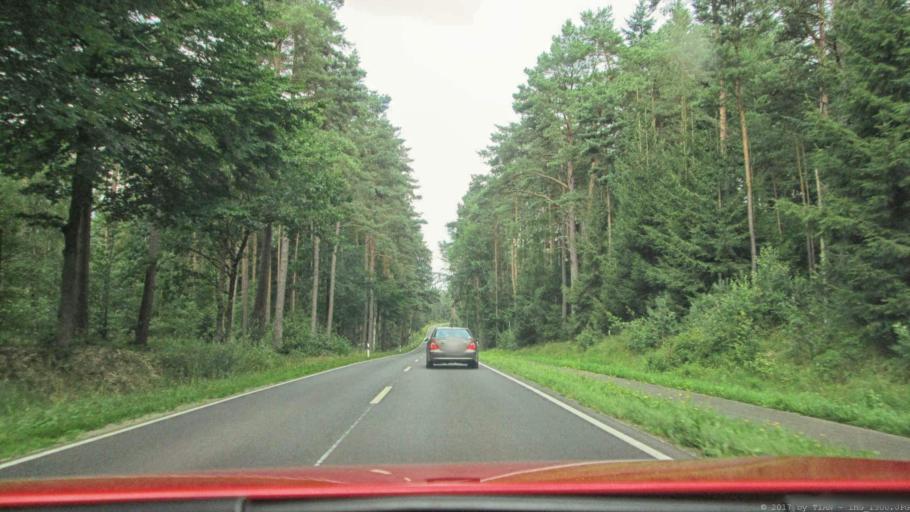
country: DE
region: Lower Saxony
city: Melbeck
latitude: 53.1513
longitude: 10.4085
